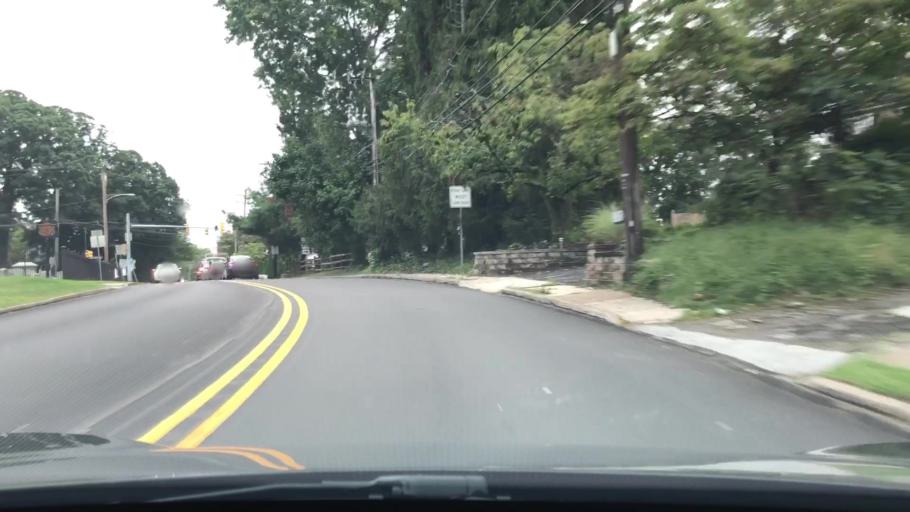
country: US
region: Pennsylvania
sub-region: Delaware County
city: Broomall
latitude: 39.9849
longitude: -75.3589
